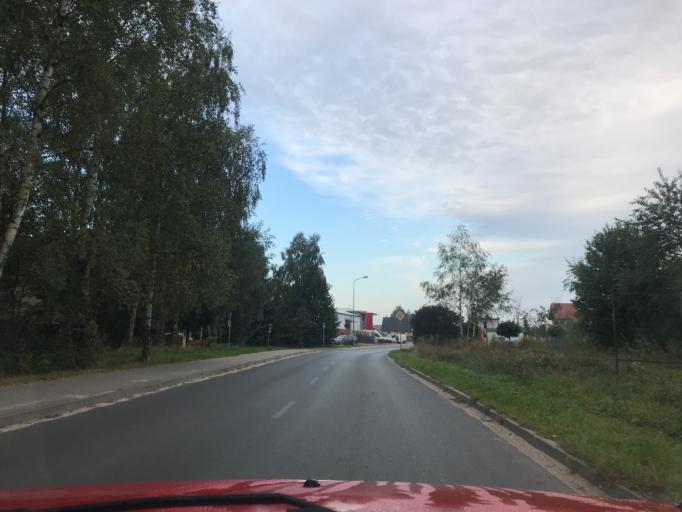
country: PL
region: Greater Poland Voivodeship
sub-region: Powiat poznanski
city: Plewiska
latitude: 52.3930
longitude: 16.7984
